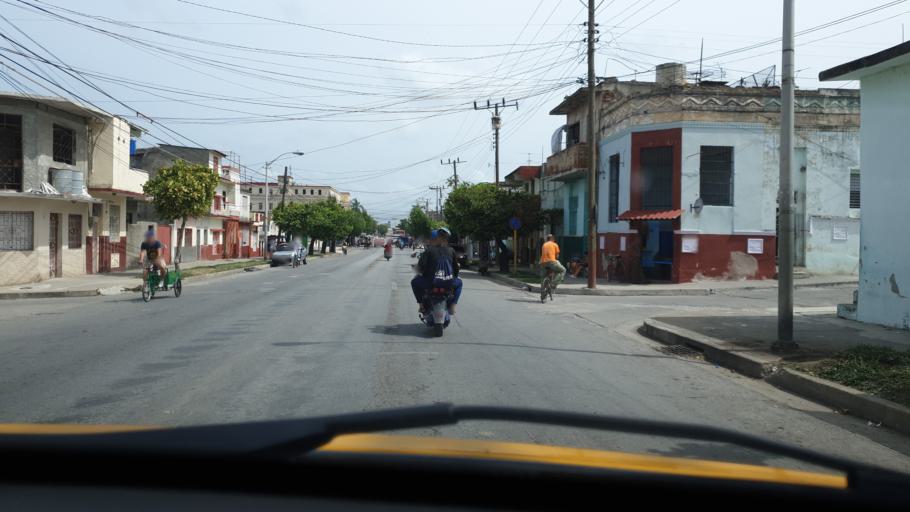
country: CU
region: Villa Clara
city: Santa Clara
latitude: 22.3971
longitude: -79.9628
